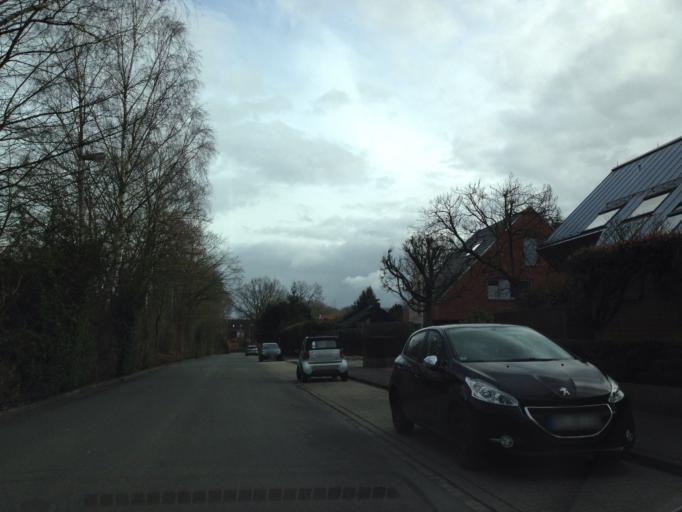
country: DE
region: North Rhine-Westphalia
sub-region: Regierungsbezirk Munster
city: Muenster
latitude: 51.9913
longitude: 7.5904
